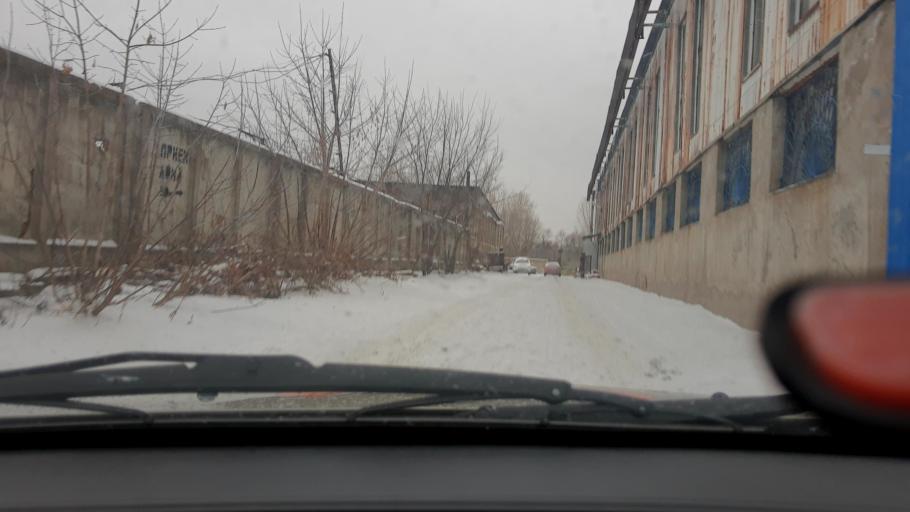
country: RU
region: Bashkortostan
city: Mikhaylovka
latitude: 54.7388
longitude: 55.8949
